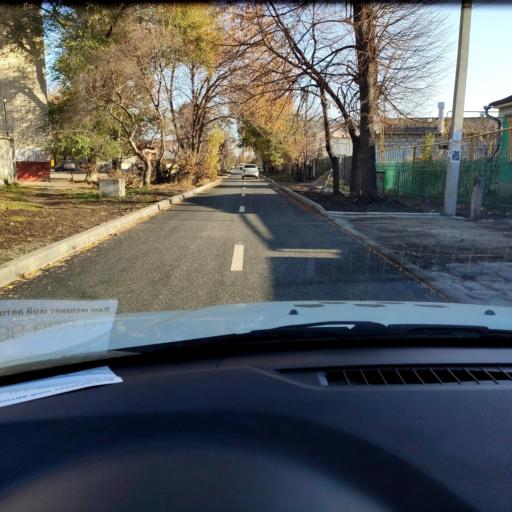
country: RU
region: Samara
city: Tol'yatti
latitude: 53.5302
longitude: 49.4163
